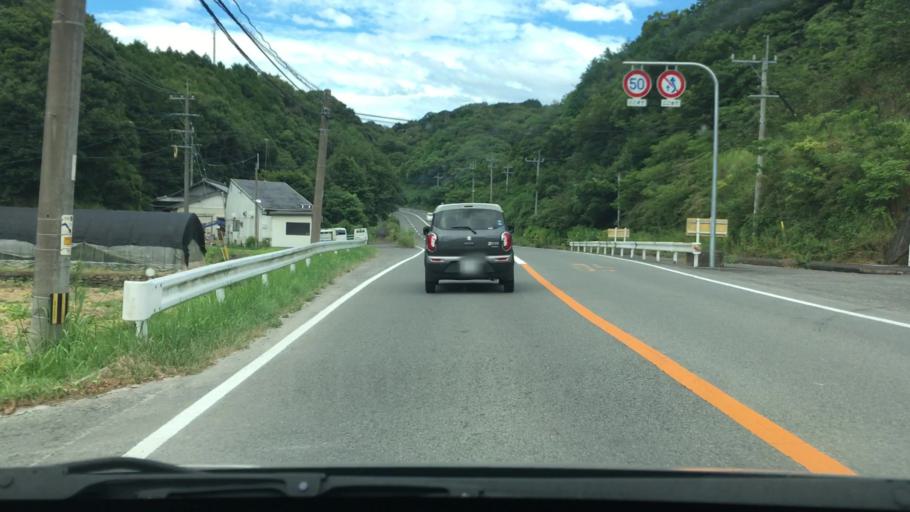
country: JP
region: Nagasaki
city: Sasebo
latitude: 32.9873
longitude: 129.7471
